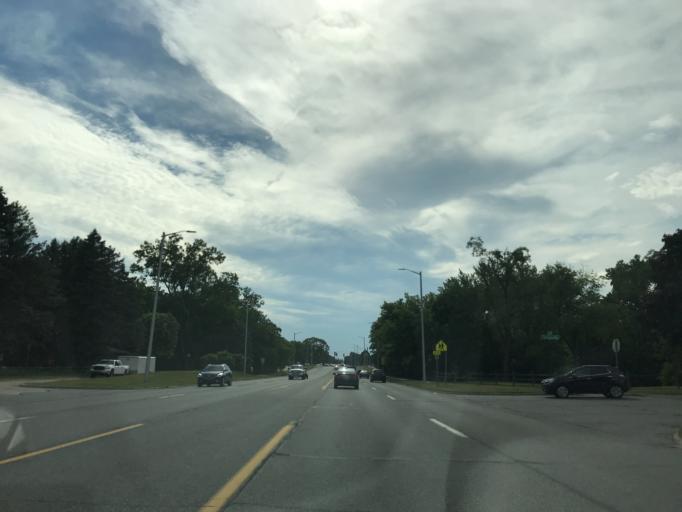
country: US
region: Michigan
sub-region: Wayne County
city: Livonia
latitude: 42.4116
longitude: -83.3772
